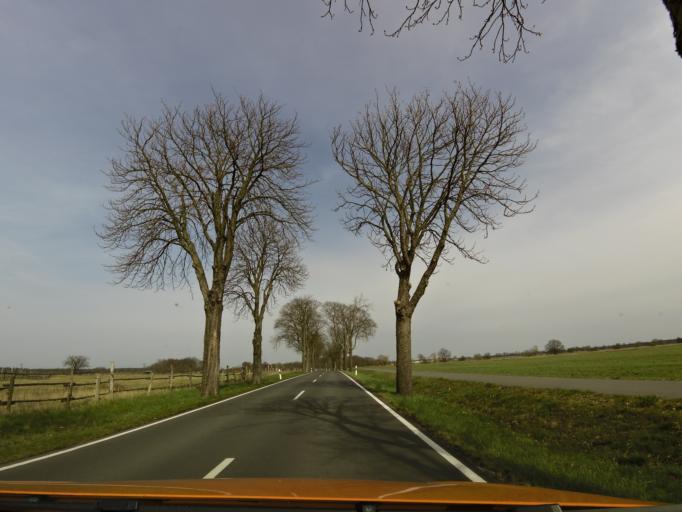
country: DE
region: Brandenburg
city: Stahnsdorf
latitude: 52.3336
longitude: 13.1816
